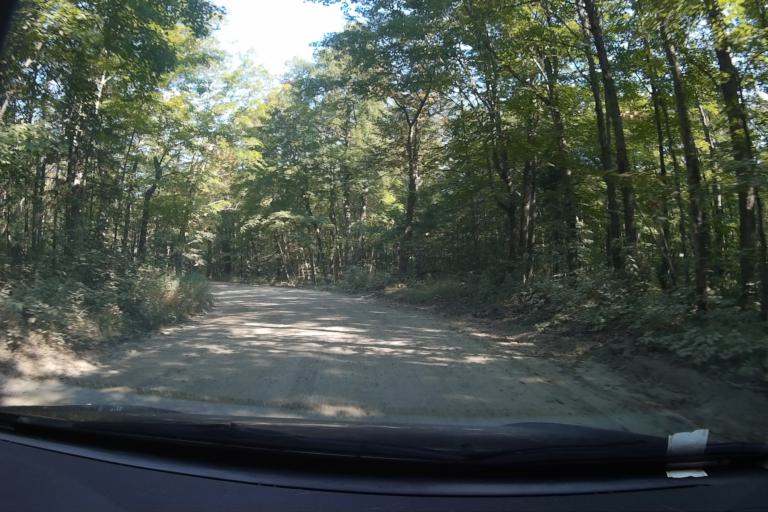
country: CA
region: Ontario
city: Huntsville
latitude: 45.5589
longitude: -78.6949
